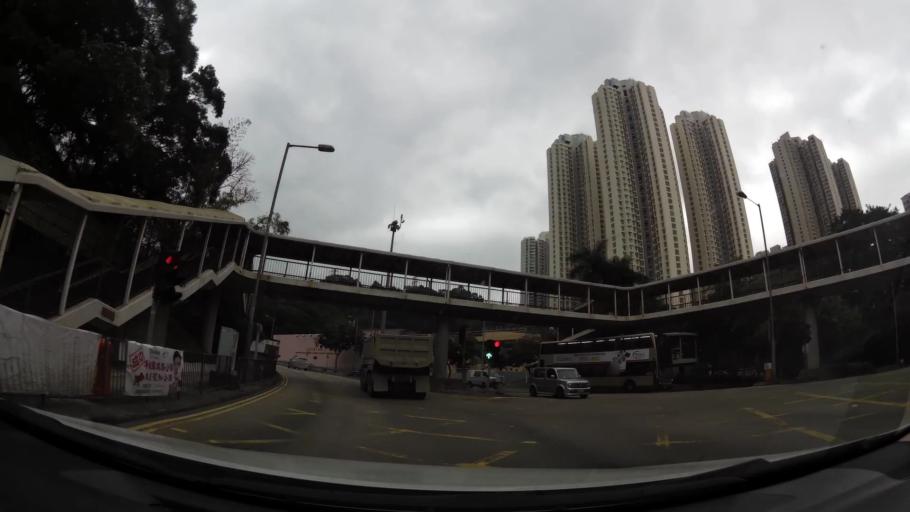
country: HK
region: Tsuen Wan
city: Tsuen Wan
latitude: 22.3721
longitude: 114.1360
